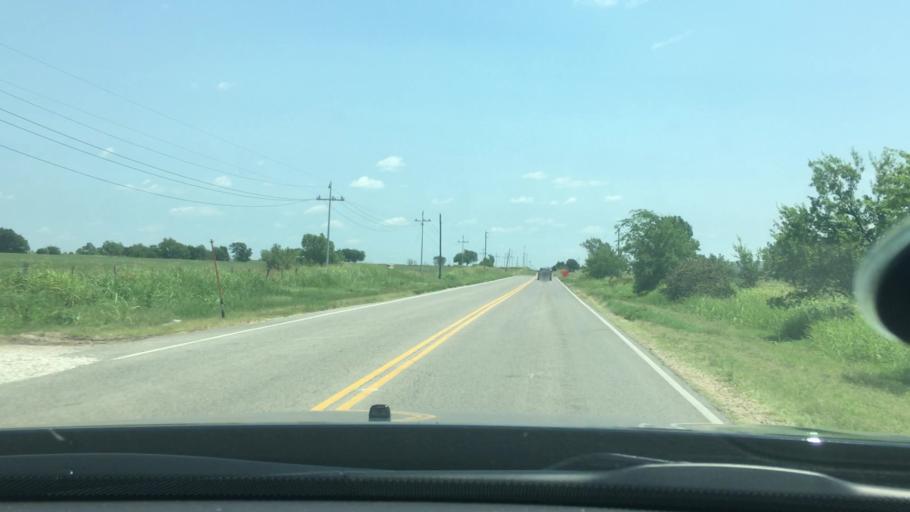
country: US
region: Oklahoma
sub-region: Garvin County
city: Stratford
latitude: 34.7967
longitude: -96.9151
